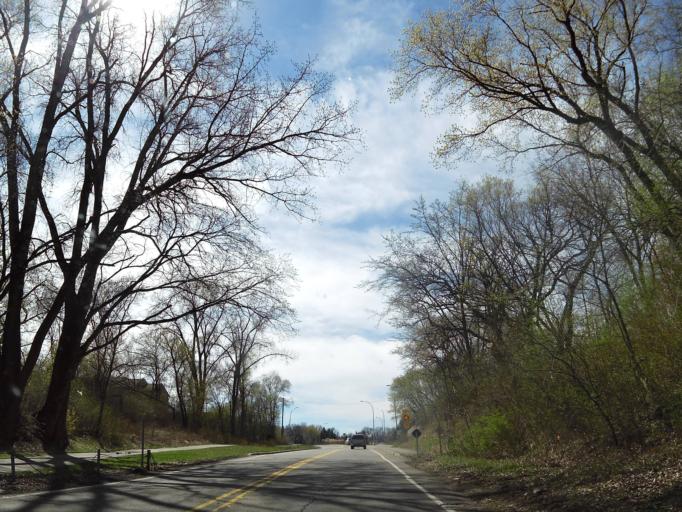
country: US
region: Minnesota
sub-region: Scott County
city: Savage
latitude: 44.7698
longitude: -93.3362
